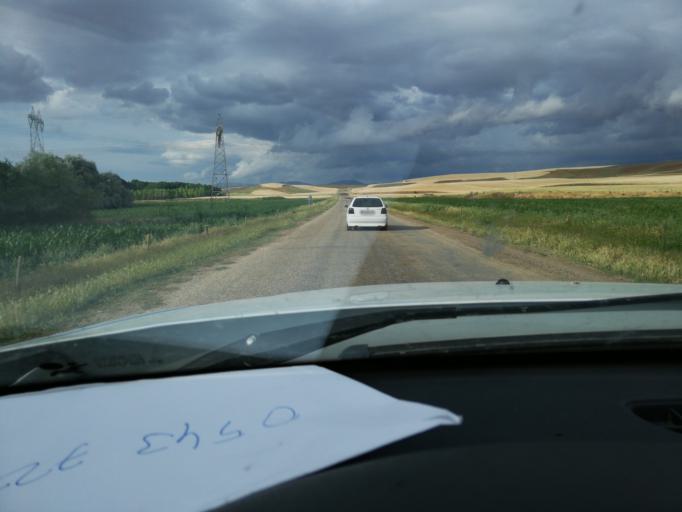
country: TR
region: Kirsehir
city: Kirsehir
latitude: 39.0283
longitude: 34.1319
